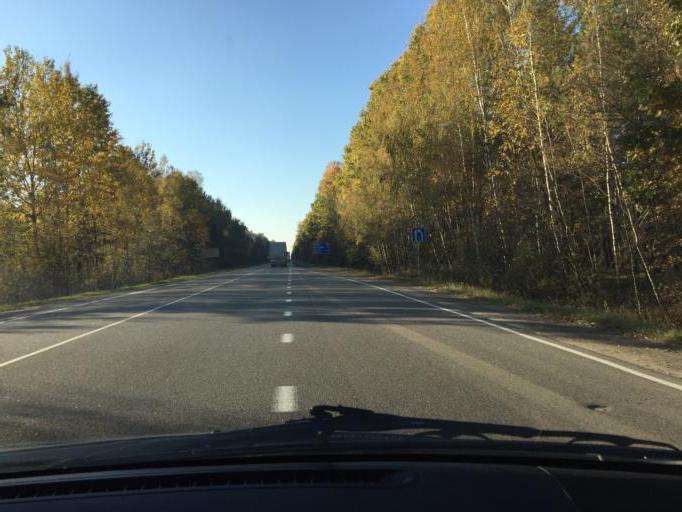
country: BY
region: Brest
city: Horad Luninyets
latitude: 52.2823
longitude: 26.8183
